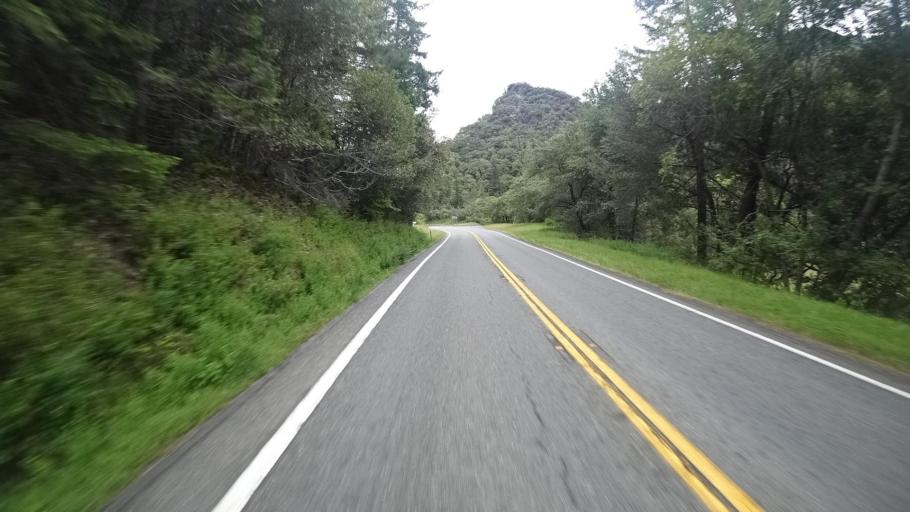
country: US
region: California
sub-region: Humboldt County
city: Willow Creek
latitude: 41.2305
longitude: -123.6592
